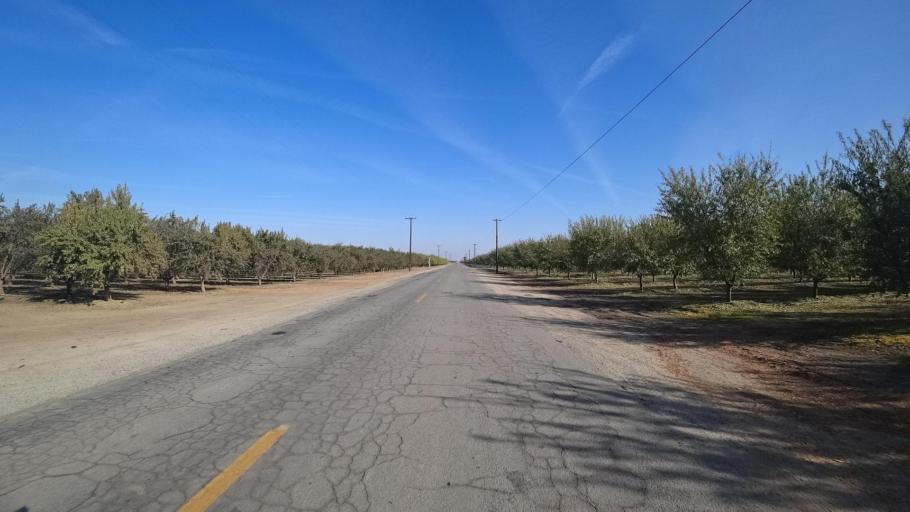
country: US
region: California
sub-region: Kern County
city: McFarland
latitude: 35.7032
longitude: -119.3270
